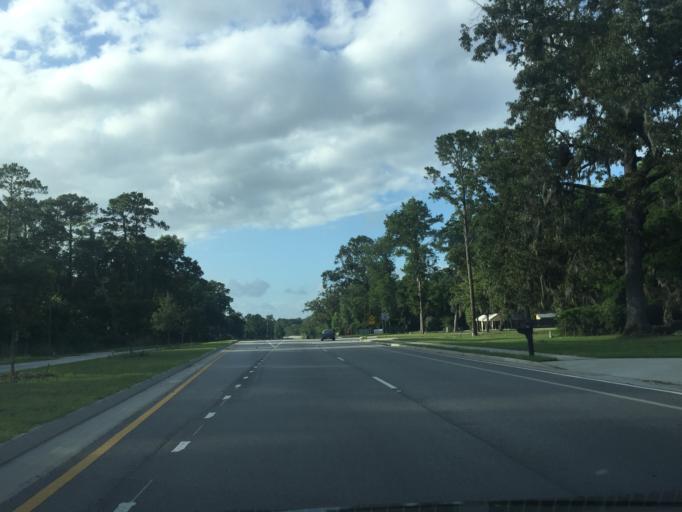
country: US
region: Georgia
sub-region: Chatham County
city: Isle of Hope
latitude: 31.9819
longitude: -81.1054
